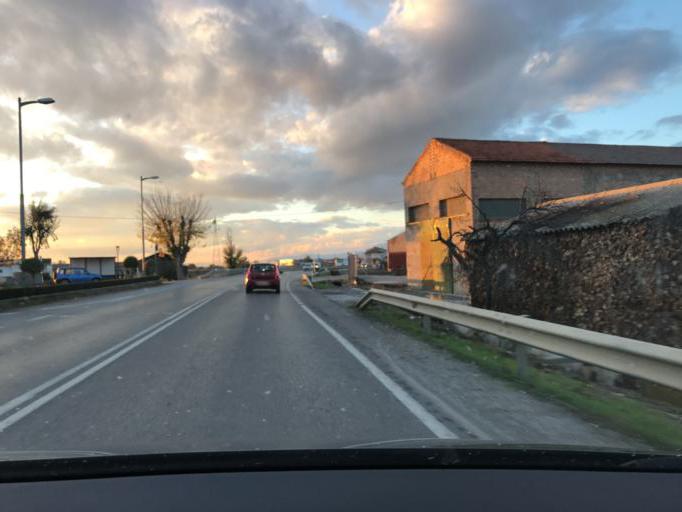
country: ES
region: Andalusia
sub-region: Provincia de Granada
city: Cullar-Vega
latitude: 37.1765
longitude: -3.6641
